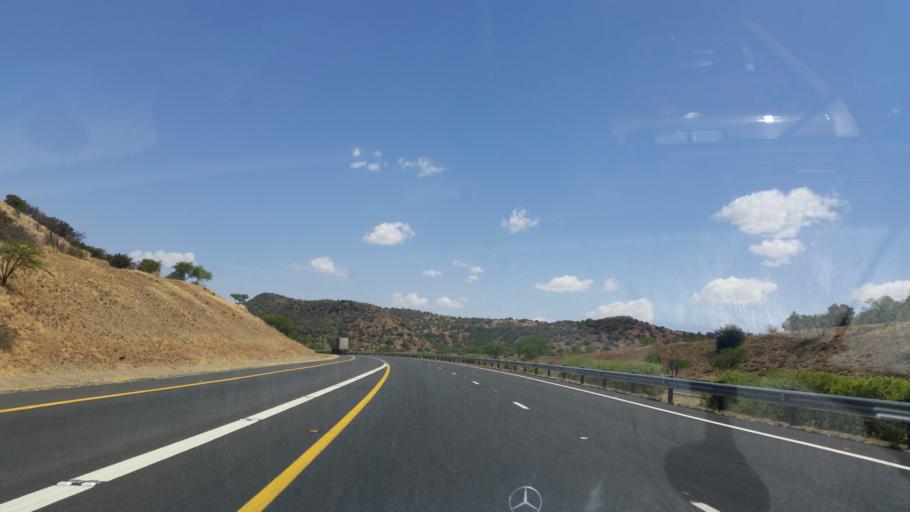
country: ZA
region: Orange Free State
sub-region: Mangaung Metropolitan Municipality
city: Bloemfontein
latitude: -28.9793
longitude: 26.2840
